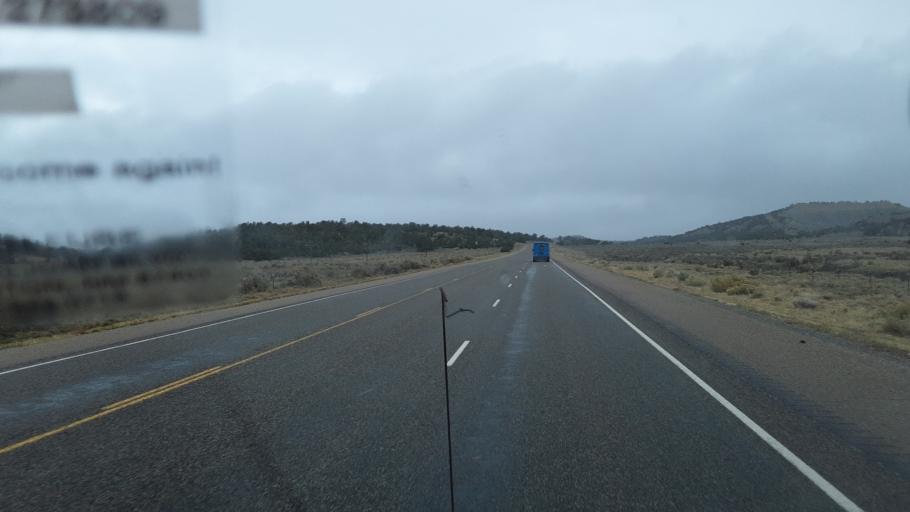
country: US
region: New Mexico
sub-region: Rio Arriba County
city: Tierra Amarilla
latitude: 36.4455
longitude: -106.4752
